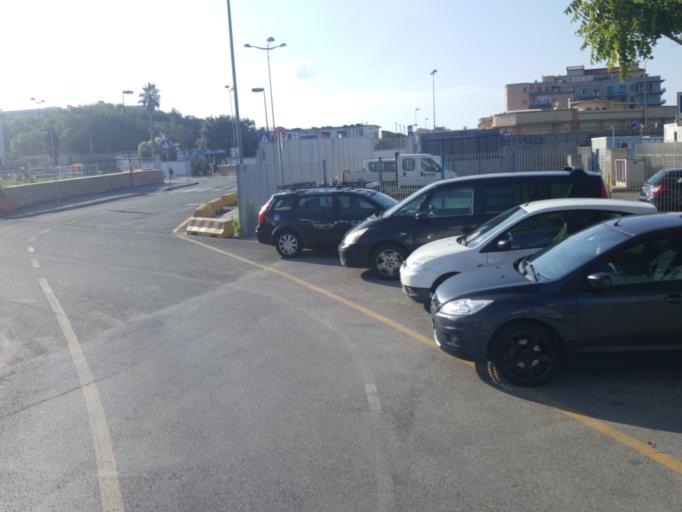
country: IT
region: Tuscany
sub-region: Provincia di Livorno
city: Livorno
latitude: 43.5425
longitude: 10.3019
